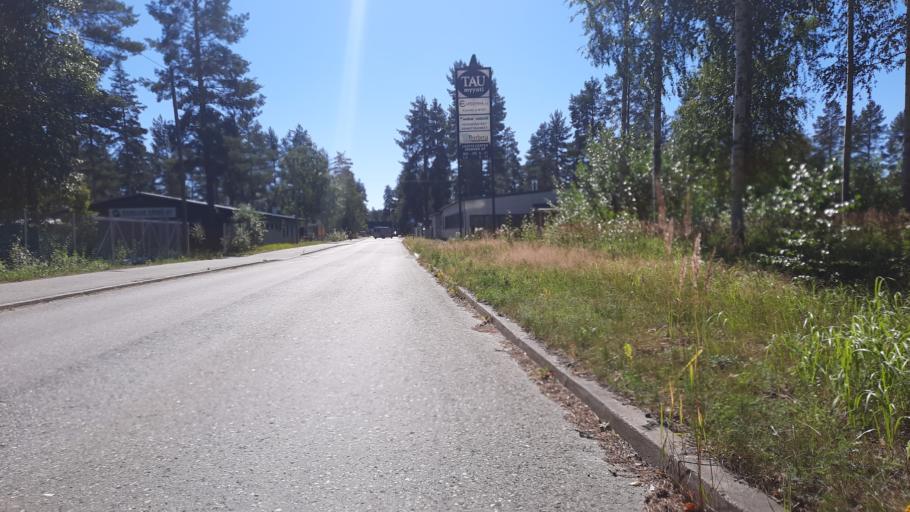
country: FI
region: North Karelia
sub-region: Joensuu
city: Joensuu
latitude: 62.6207
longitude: 29.7430
